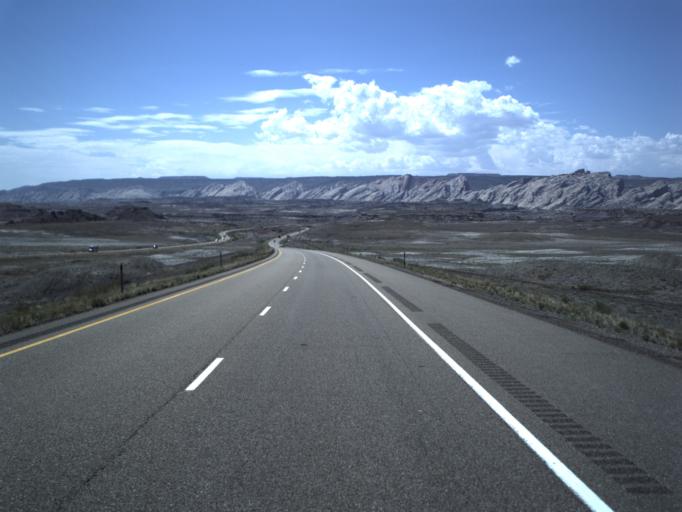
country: US
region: Utah
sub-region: Carbon County
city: East Carbon City
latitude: 38.9385
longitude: -110.3427
